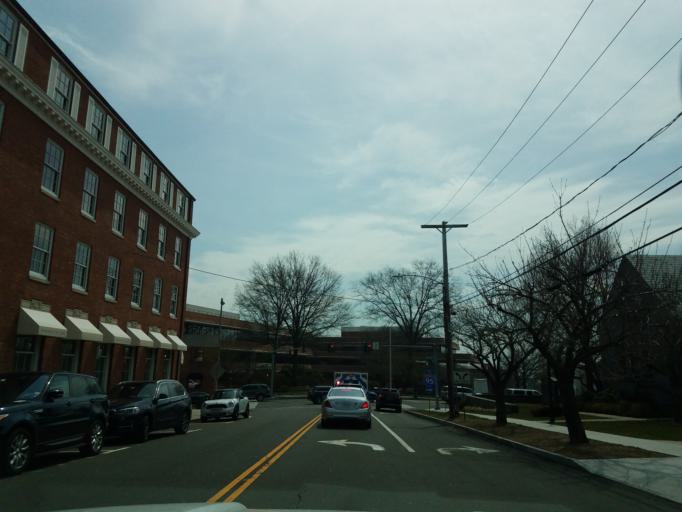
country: US
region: Connecticut
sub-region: Fairfield County
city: Greenwich
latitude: 41.0317
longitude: -73.6273
